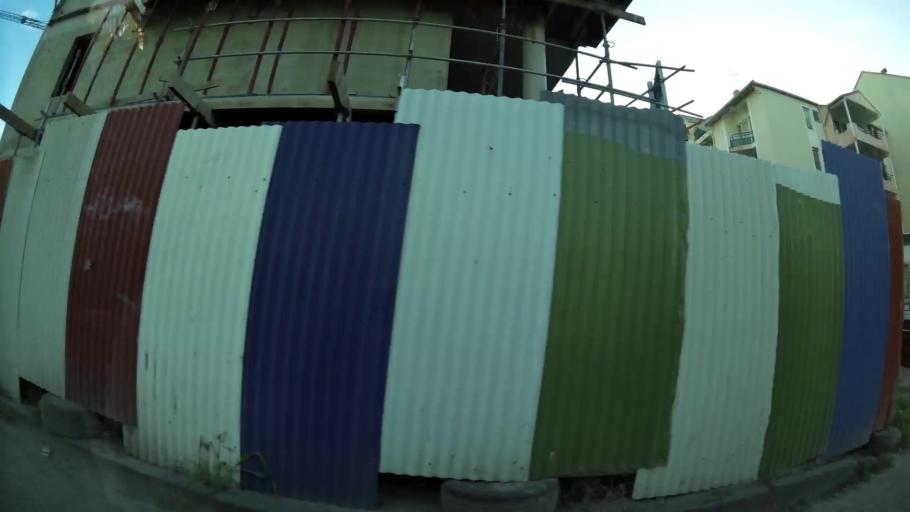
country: GP
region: Guadeloupe
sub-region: Guadeloupe
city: Pointe-a-Pitre
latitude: 16.2325
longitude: -61.5316
